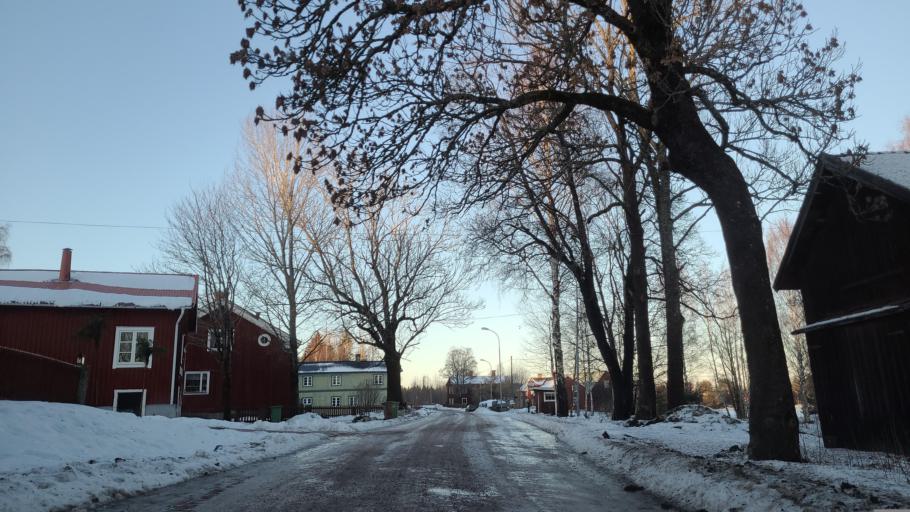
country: SE
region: Gaevleborg
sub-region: Soderhamns Kommun
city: Soderhamn
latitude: 61.2726
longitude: 16.9937
